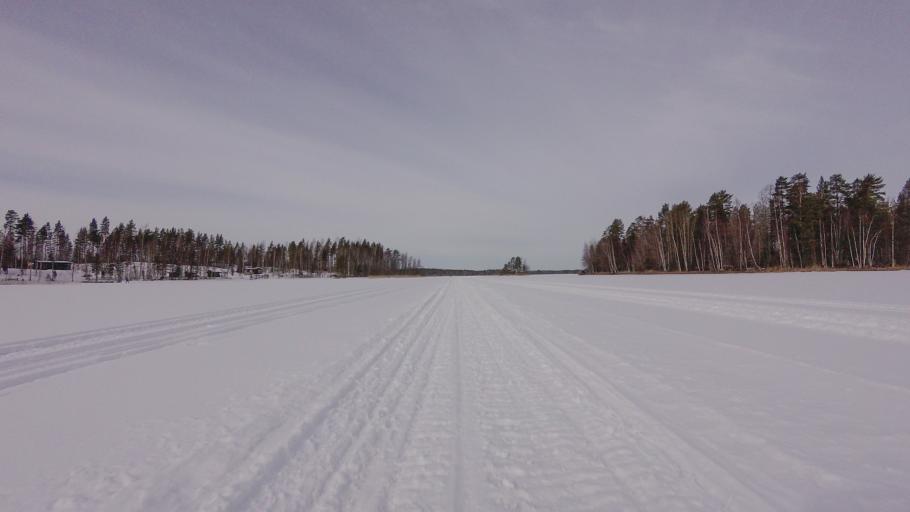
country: FI
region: Southern Savonia
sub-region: Savonlinna
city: Heinaevesi
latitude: 62.1237
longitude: 28.6110
